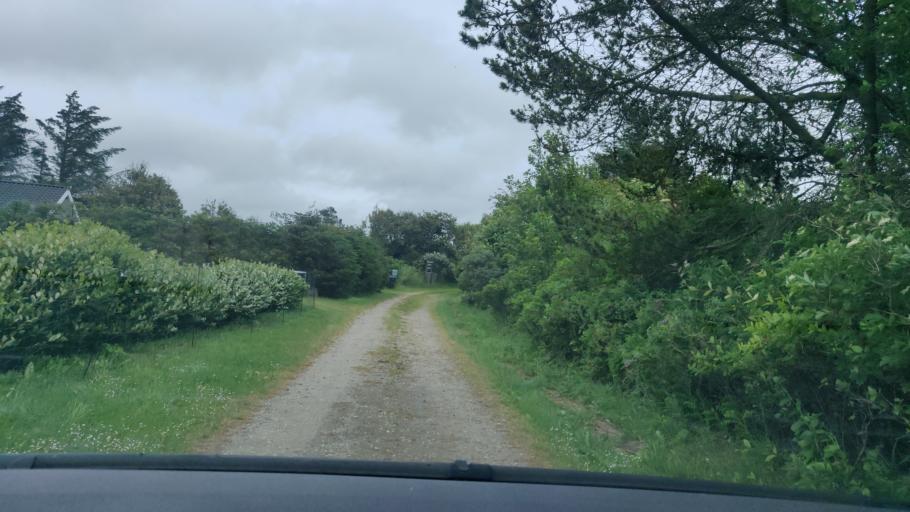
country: DK
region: North Denmark
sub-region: Jammerbugt Kommune
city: Pandrup
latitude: 57.2570
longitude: 9.6036
